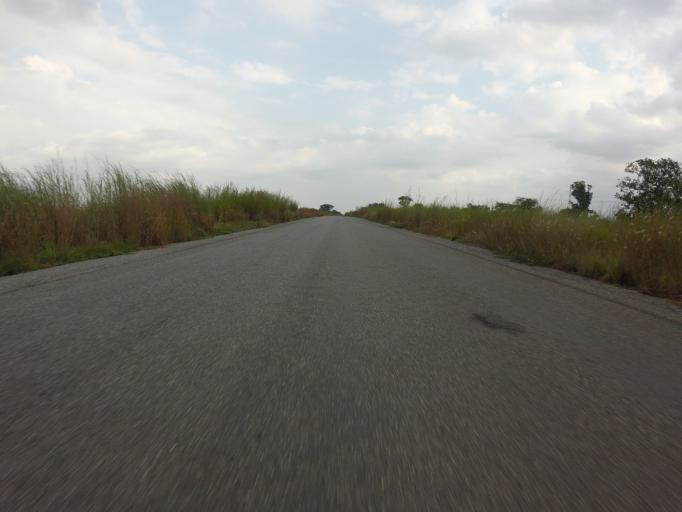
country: GH
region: Volta
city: Ho
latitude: 6.4217
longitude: 0.5192
